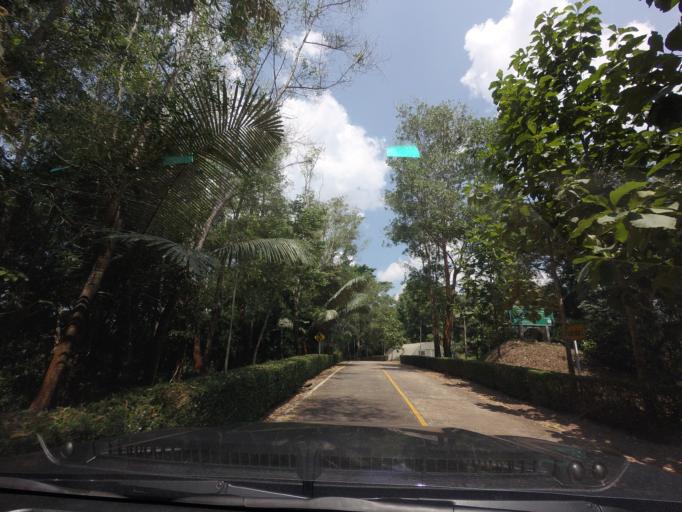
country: TH
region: Nan
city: Bo Kluea
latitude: 19.0213
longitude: 101.2079
